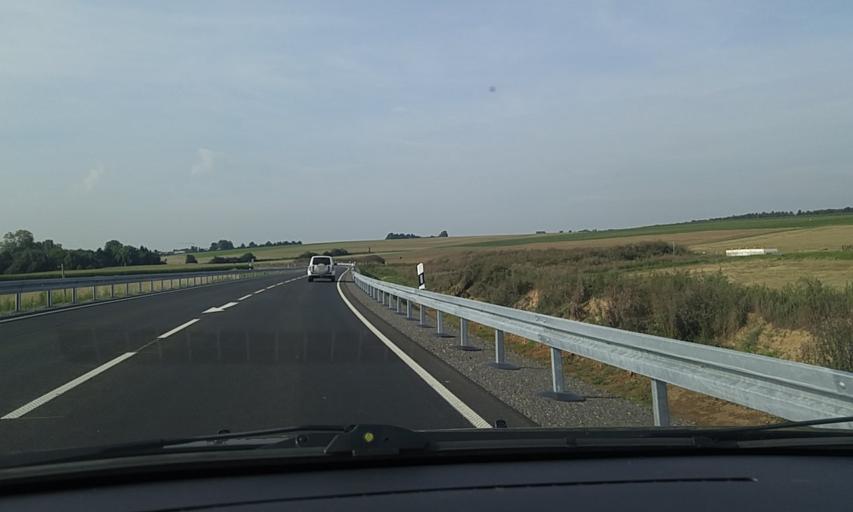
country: DE
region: Hesse
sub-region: Regierungsbezirk Darmstadt
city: Karben
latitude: 50.2678
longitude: 8.7586
